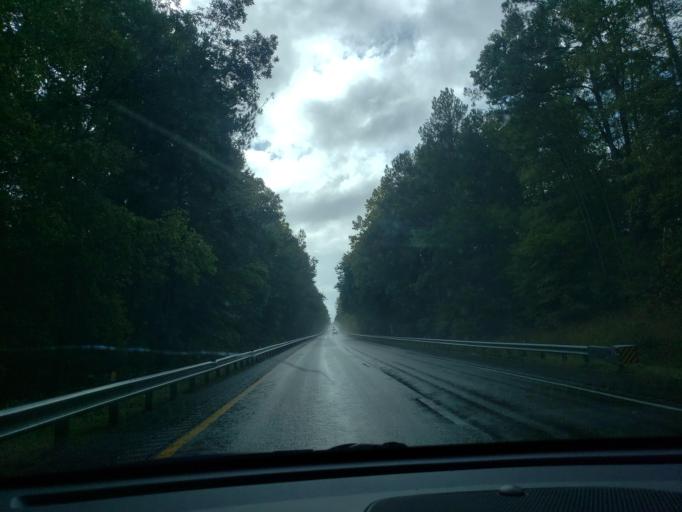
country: US
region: Virginia
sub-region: Dinwiddie County
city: Dinwiddie
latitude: 37.0134
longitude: -77.6585
